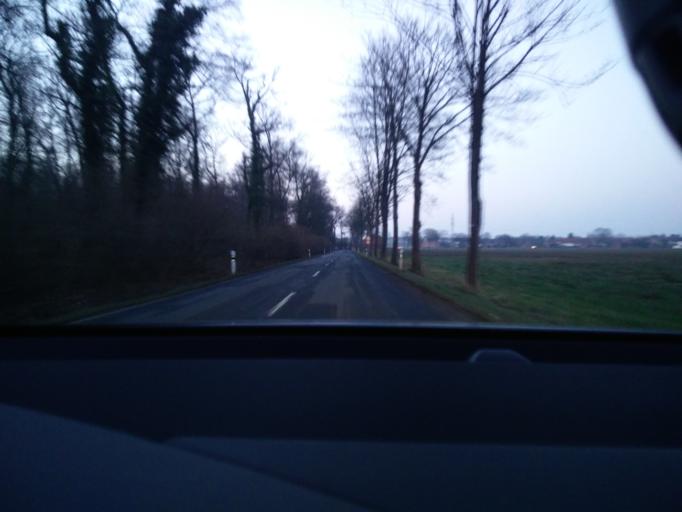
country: DE
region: Lower Saxony
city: Laatzen
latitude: 52.3204
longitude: 9.8532
